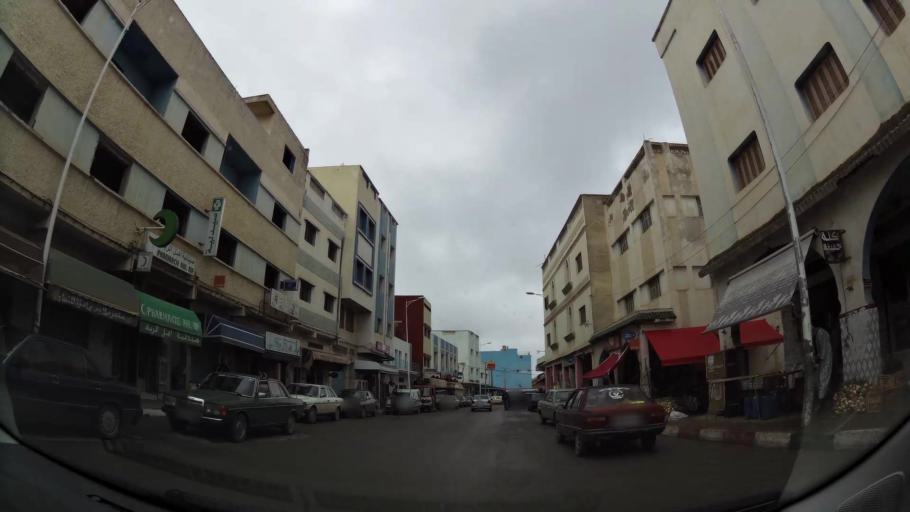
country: MA
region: Oriental
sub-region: Nador
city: Midar
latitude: 35.0460
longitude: -3.4525
